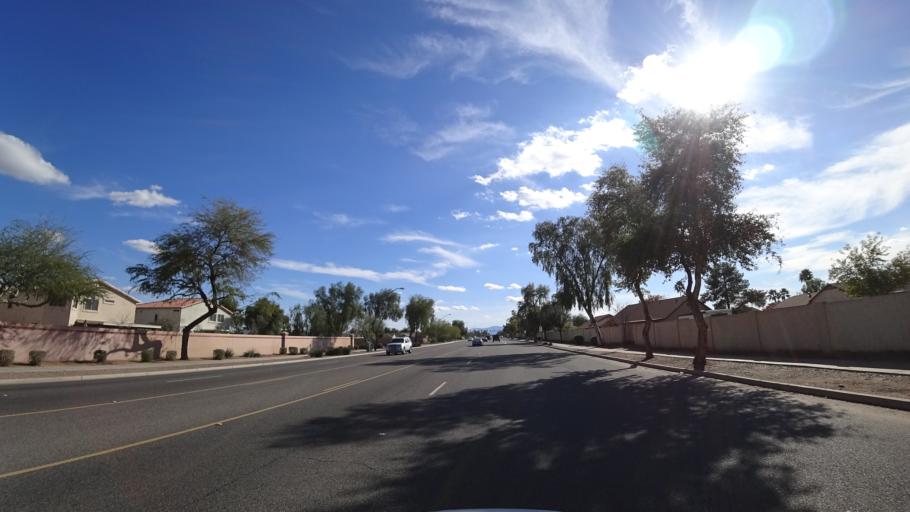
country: US
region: Arizona
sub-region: Maricopa County
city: Glendale
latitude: 33.5191
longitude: -112.2206
